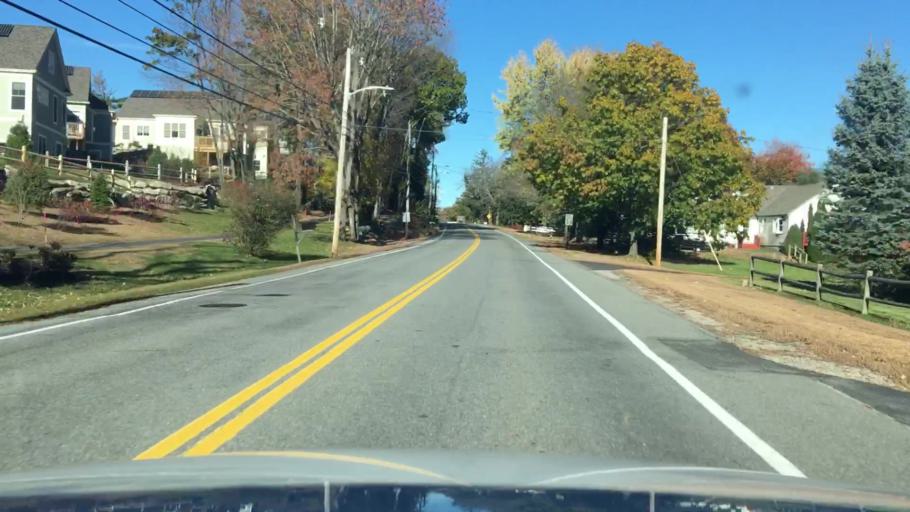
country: US
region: Maine
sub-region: Cumberland County
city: Falmouth
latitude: 43.7220
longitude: -70.2466
